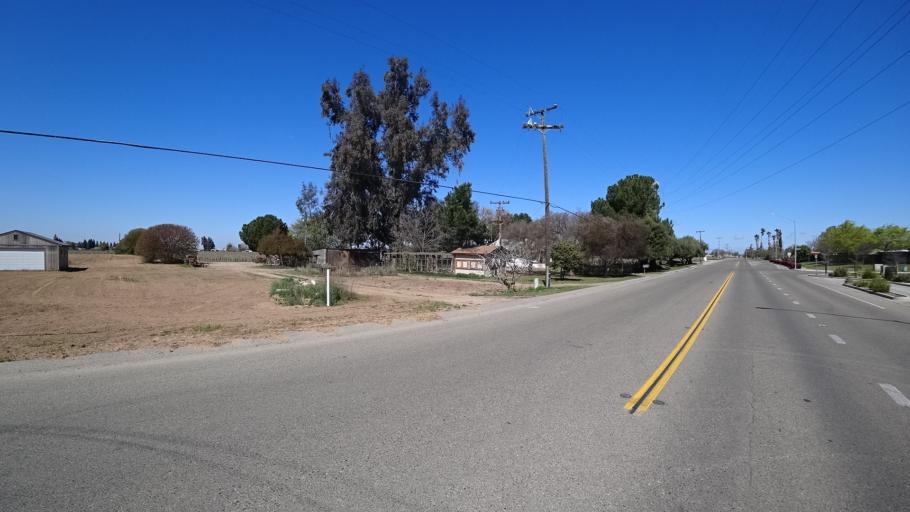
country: US
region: California
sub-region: Fresno County
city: West Park
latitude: 36.7844
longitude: -119.8984
